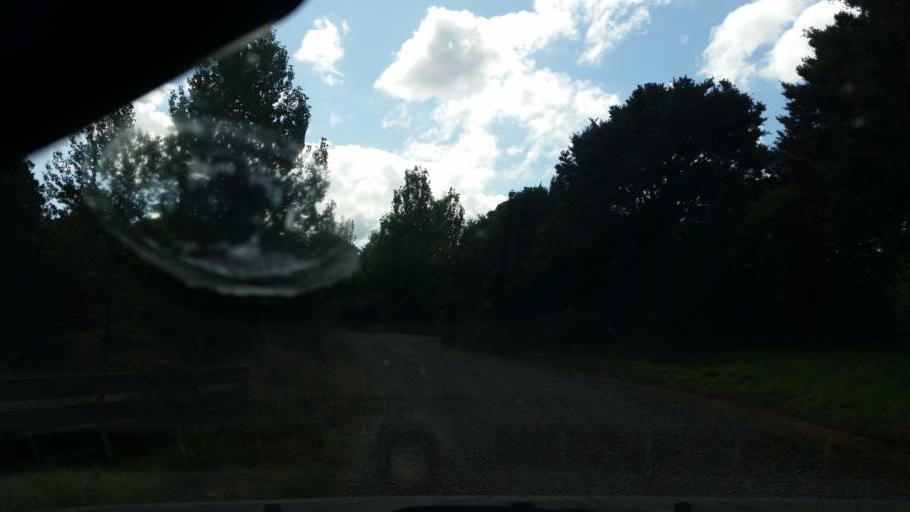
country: NZ
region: Northland
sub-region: Kaipara District
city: Dargaville
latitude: -35.7082
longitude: 173.6043
